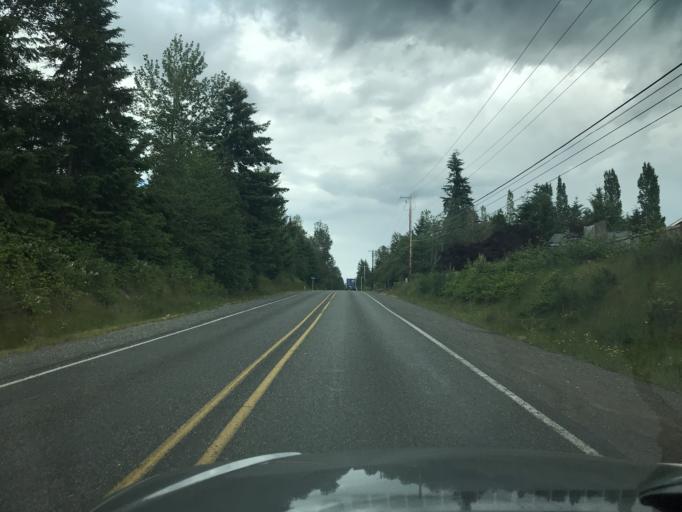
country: US
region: Washington
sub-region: Pierce County
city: Prairie Ridge
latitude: 47.1475
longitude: -122.1641
